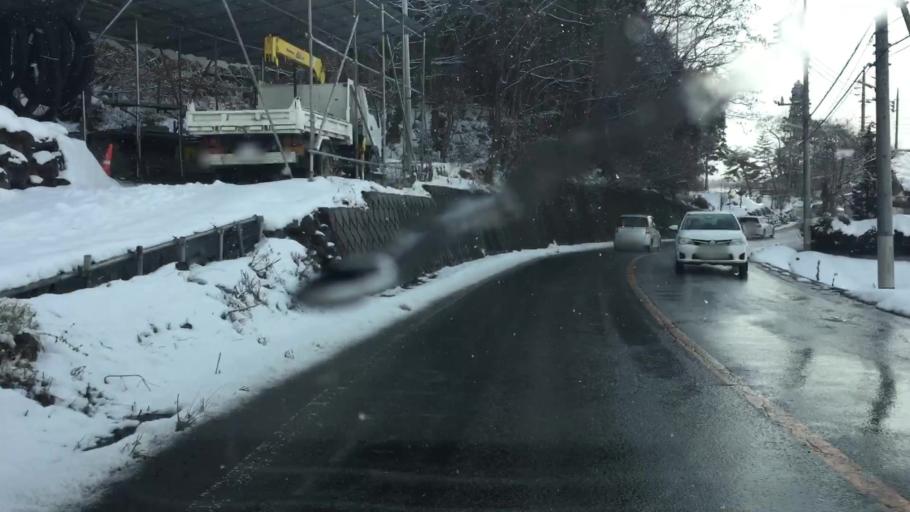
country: JP
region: Gunma
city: Numata
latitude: 36.6744
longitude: 139.0631
